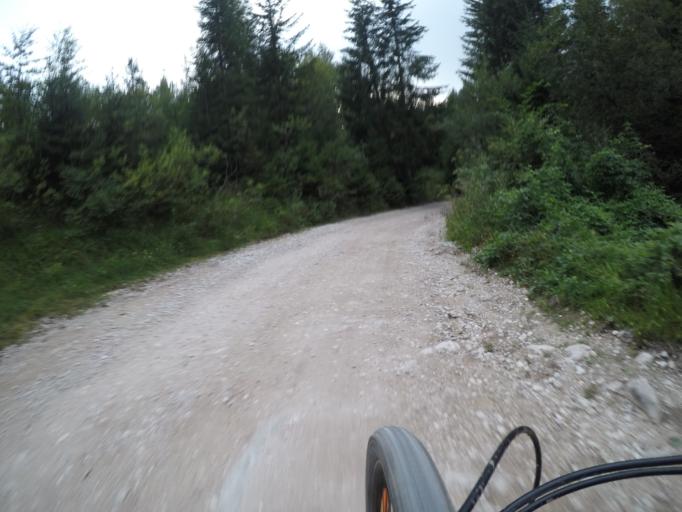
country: IT
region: Veneto
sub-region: Provincia di Vicenza
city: Gallio
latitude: 45.9003
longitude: 11.5261
